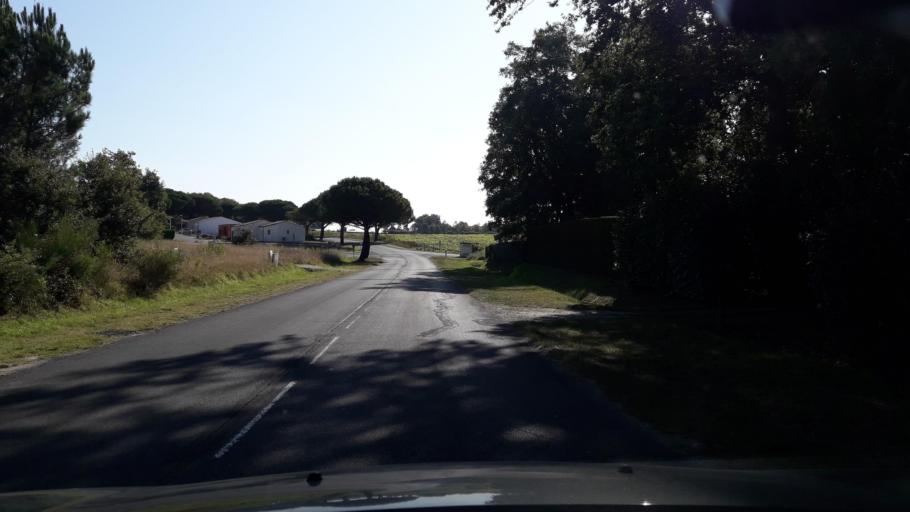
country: FR
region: Poitou-Charentes
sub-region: Departement de la Charente-Maritime
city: Les Mathes
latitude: 45.7130
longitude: -1.1379
